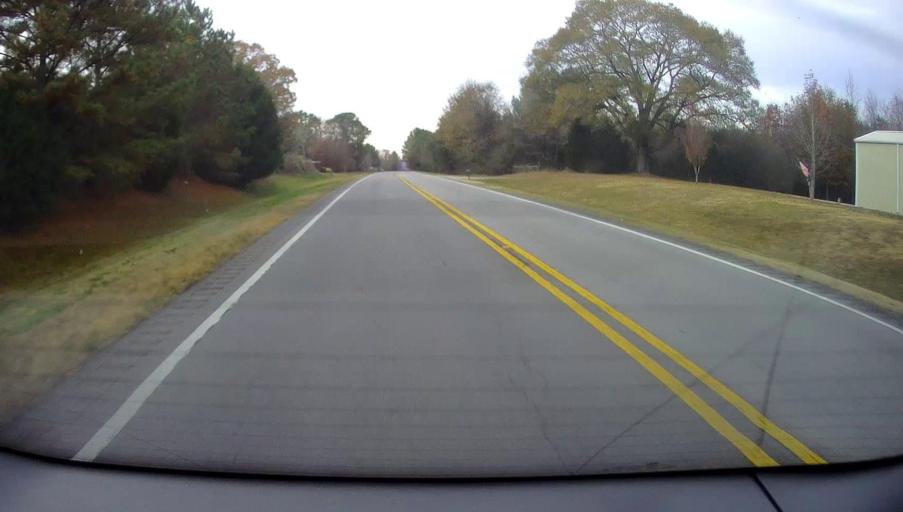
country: US
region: Alabama
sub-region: Marshall County
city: Arab
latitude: 34.3891
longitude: -86.6679
